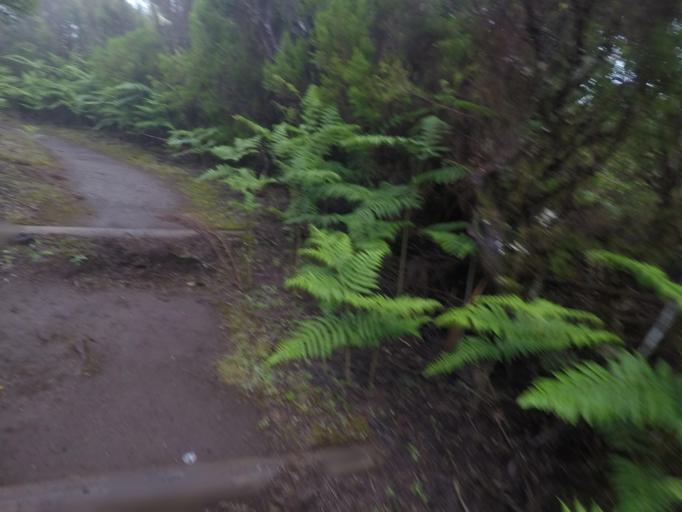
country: PT
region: Madeira
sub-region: Calheta
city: Arco da Calheta
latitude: 32.7746
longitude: -17.1235
